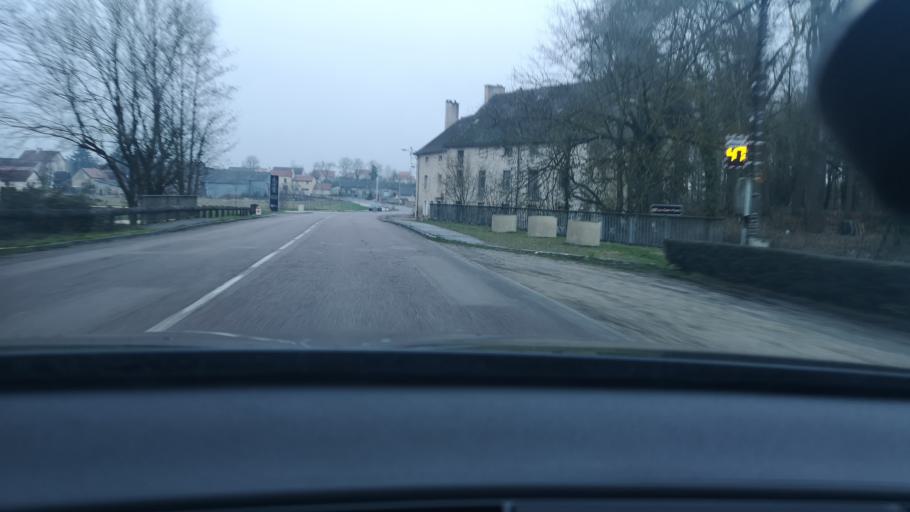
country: FR
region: Bourgogne
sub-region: Departement de la Cote-d'Or
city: Fenay
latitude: 47.2257
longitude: 5.0631
